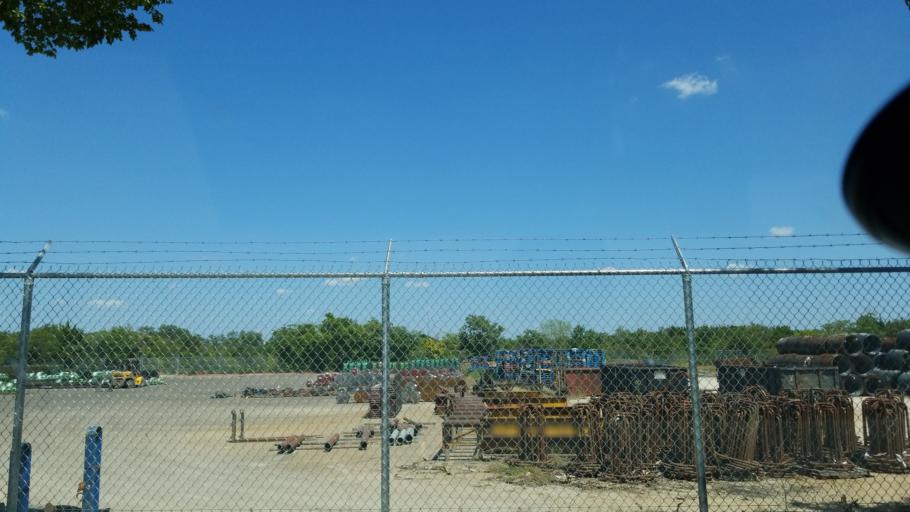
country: US
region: Texas
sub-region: Dallas County
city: Cockrell Hill
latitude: 32.7174
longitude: -96.8849
